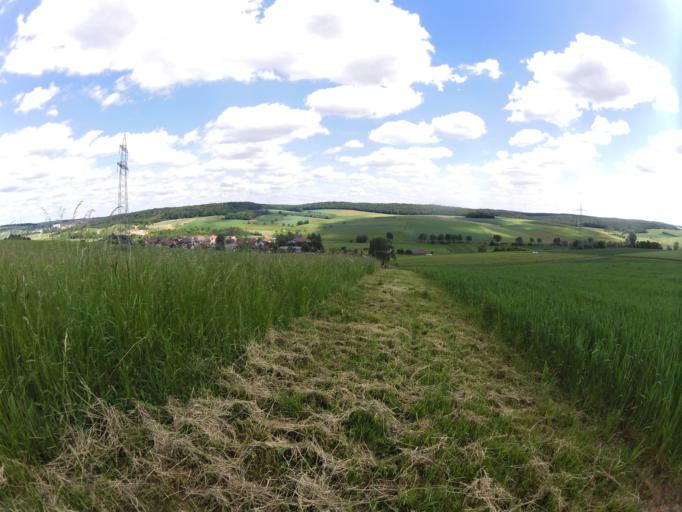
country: DE
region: Bavaria
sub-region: Regierungsbezirk Unterfranken
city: Uettingen
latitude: 49.7780
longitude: 9.7645
